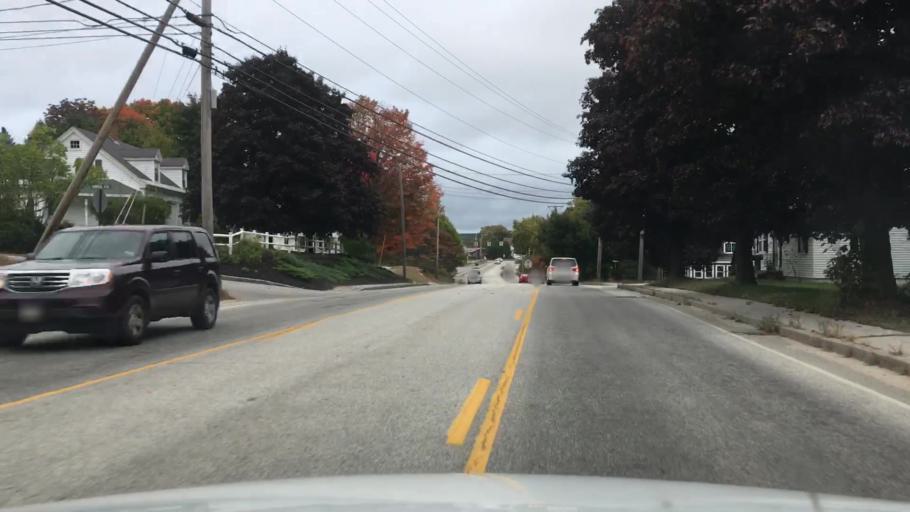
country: US
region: Maine
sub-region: Oxford County
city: Norway
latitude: 44.2044
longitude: -70.5317
